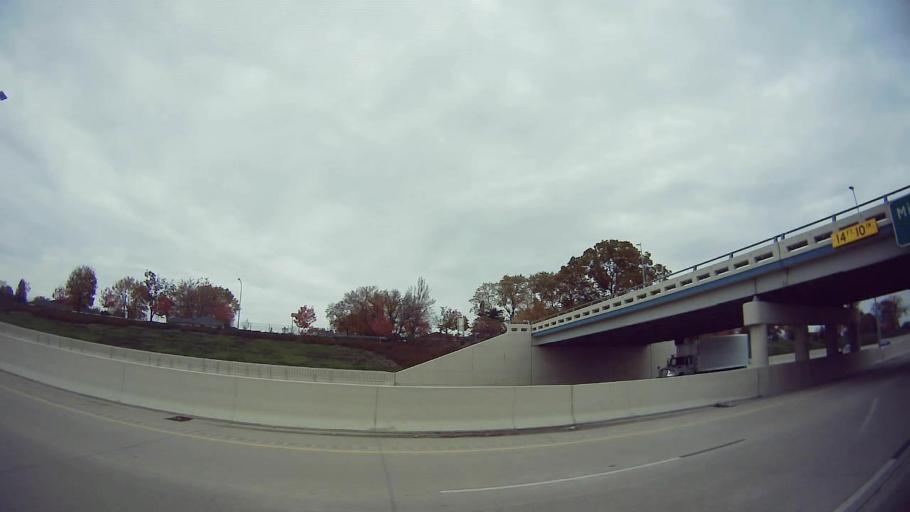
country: US
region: Michigan
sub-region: Wayne County
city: Livonia
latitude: 42.3826
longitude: -83.3632
